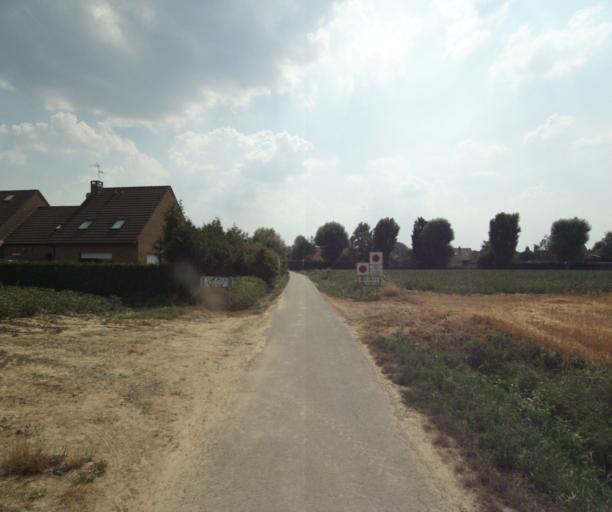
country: FR
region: Nord-Pas-de-Calais
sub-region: Departement du Nord
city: Quesnoy-sur-Deule
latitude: 50.7213
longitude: 3.0002
